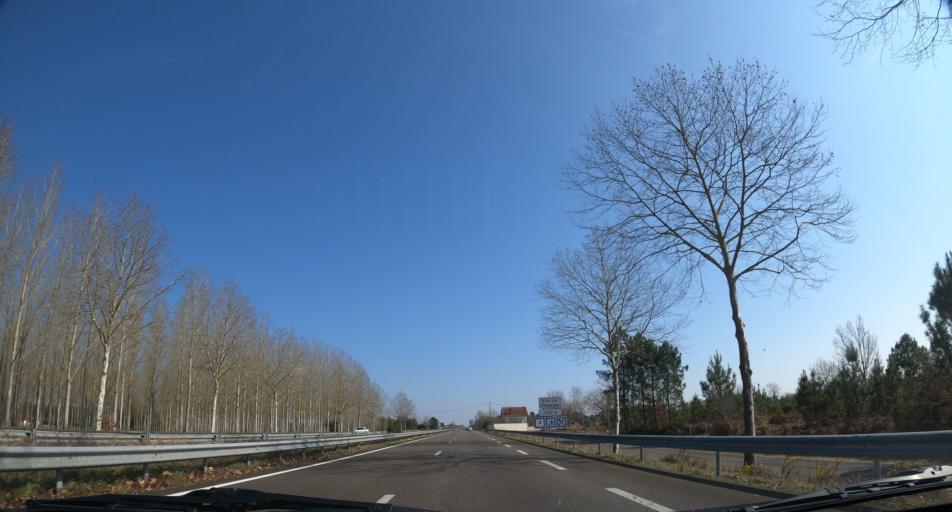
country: FR
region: Aquitaine
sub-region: Departement des Landes
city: Tartas
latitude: 43.8407
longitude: -0.7664
